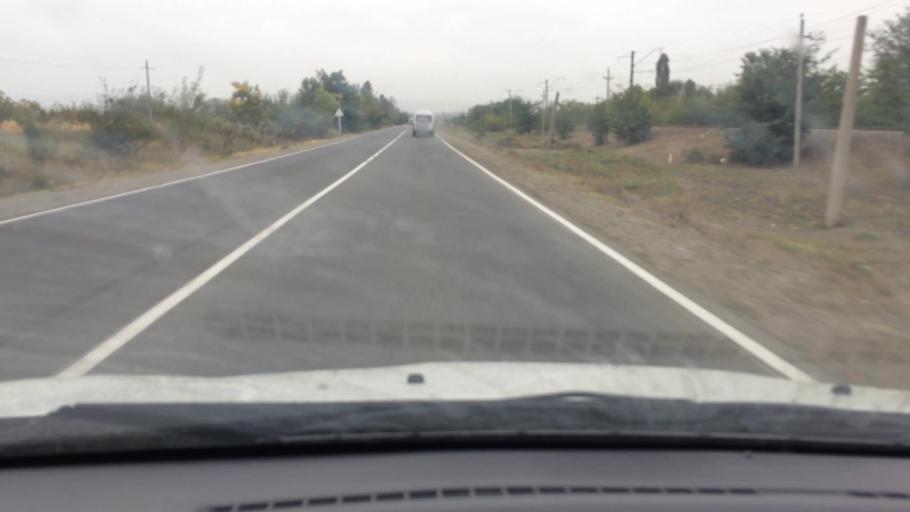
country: GE
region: Kvemo Kartli
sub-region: Marneuli
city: Marneuli
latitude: 41.4514
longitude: 44.8134
